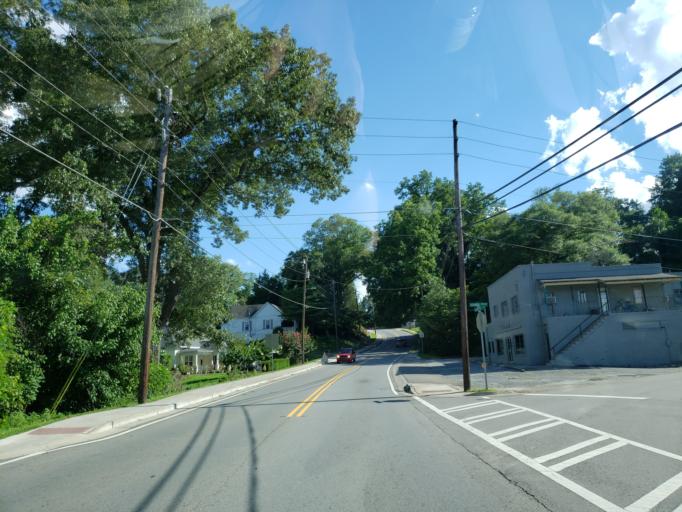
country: US
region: Georgia
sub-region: Cherokee County
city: Canton
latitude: 34.2269
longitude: -84.4931
